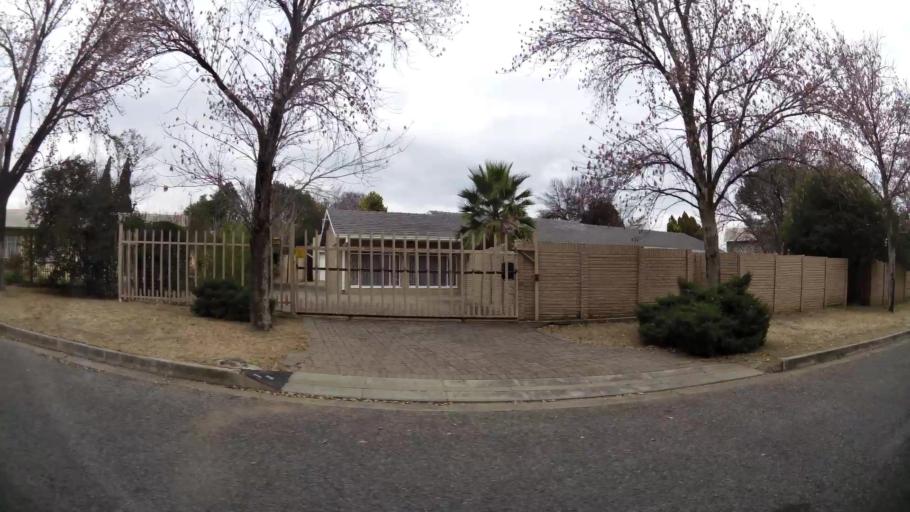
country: ZA
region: Orange Free State
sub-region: Fezile Dabi District Municipality
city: Kroonstad
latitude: -27.6721
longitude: 27.2511
